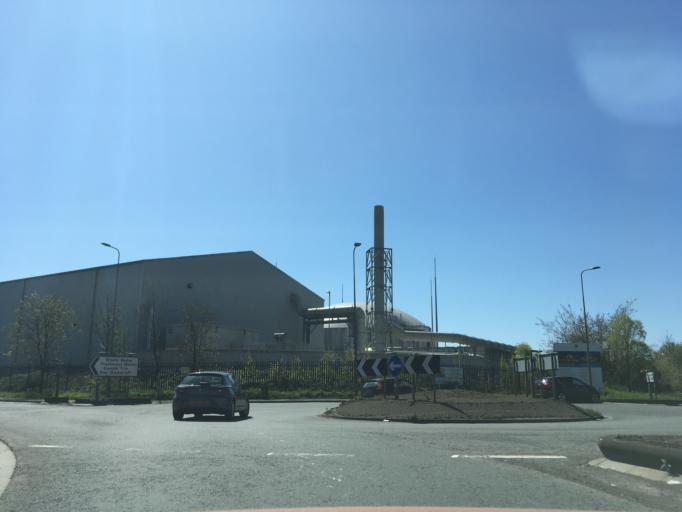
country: GB
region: Wales
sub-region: Cardiff
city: Cardiff
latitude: 51.4783
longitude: -3.1372
